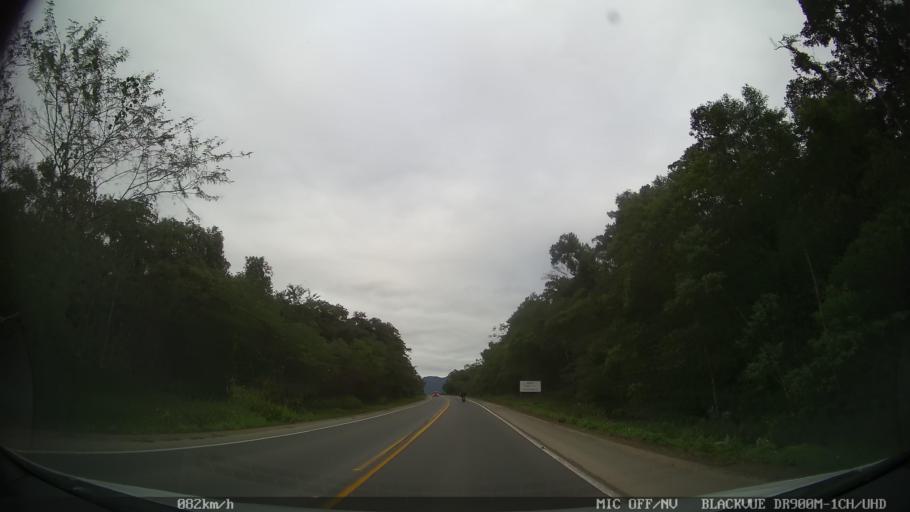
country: BR
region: Santa Catarina
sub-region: Joinville
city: Joinville
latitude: -26.2628
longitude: -48.9159
